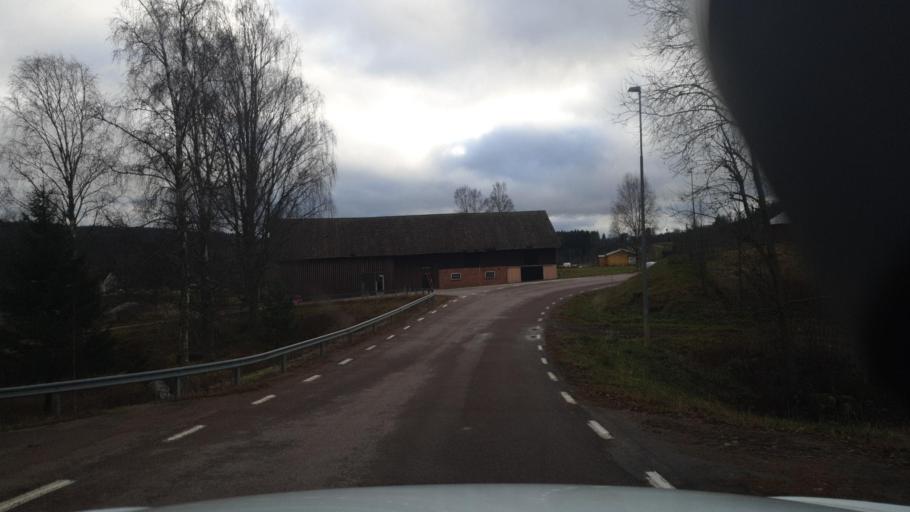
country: SE
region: Vaermland
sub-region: Arvika Kommun
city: Arvika
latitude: 59.7744
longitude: 12.8227
